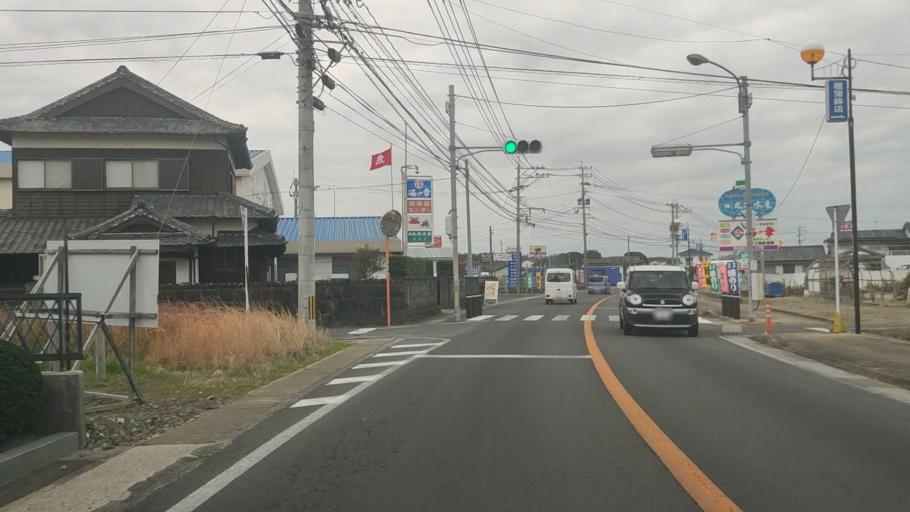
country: JP
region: Nagasaki
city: Shimabara
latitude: 32.8593
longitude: 130.3286
